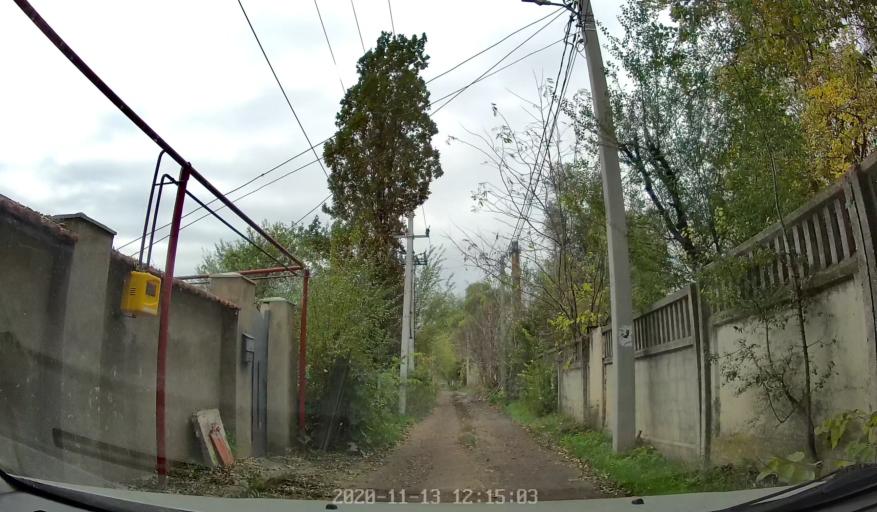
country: MD
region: Laloveni
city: Ialoveni
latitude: 46.9518
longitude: 28.8377
